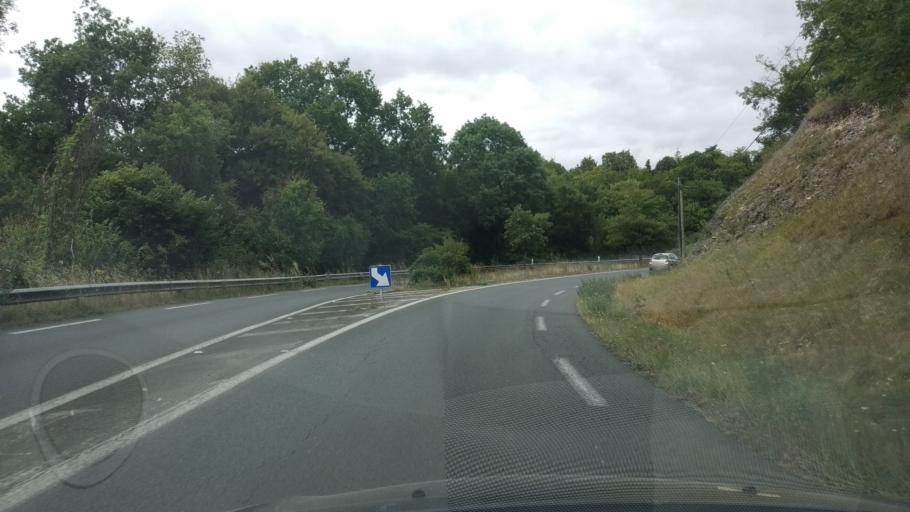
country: FR
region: Poitou-Charentes
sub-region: Departement de la Vienne
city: Saint-Benoit
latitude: 46.5545
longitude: 0.3499
